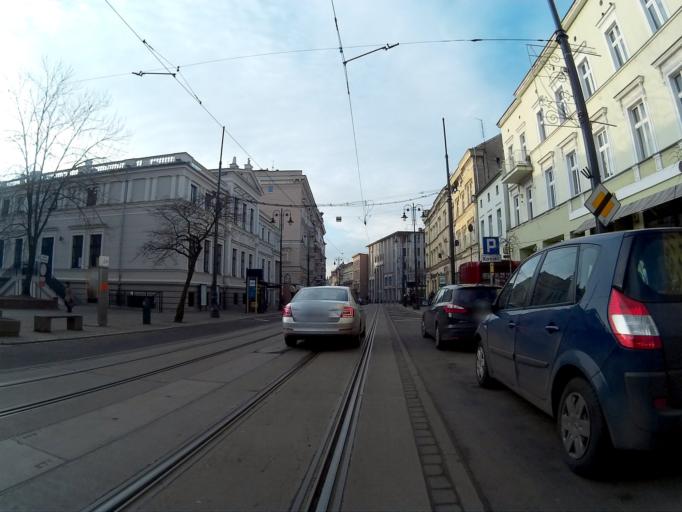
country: PL
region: Kujawsko-Pomorskie
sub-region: Bydgoszcz
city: Bydgoszcz
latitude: 53.1269
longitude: 18.0044
